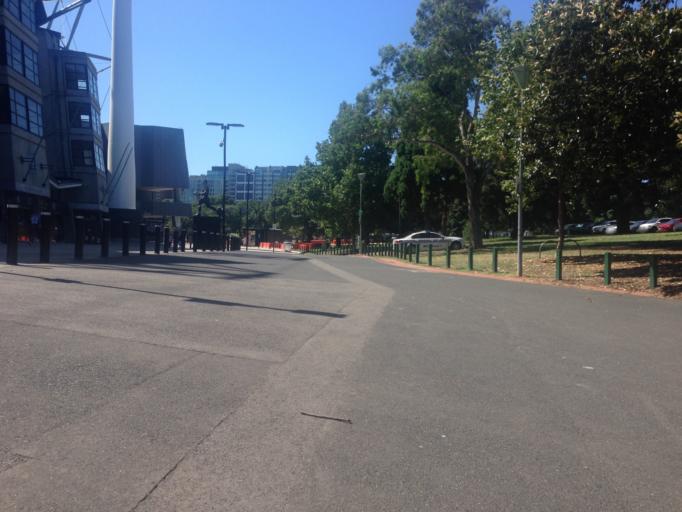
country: AU
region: Victoria
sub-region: Melbourne
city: East Melbourne
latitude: -37.8203
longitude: 144.9852
